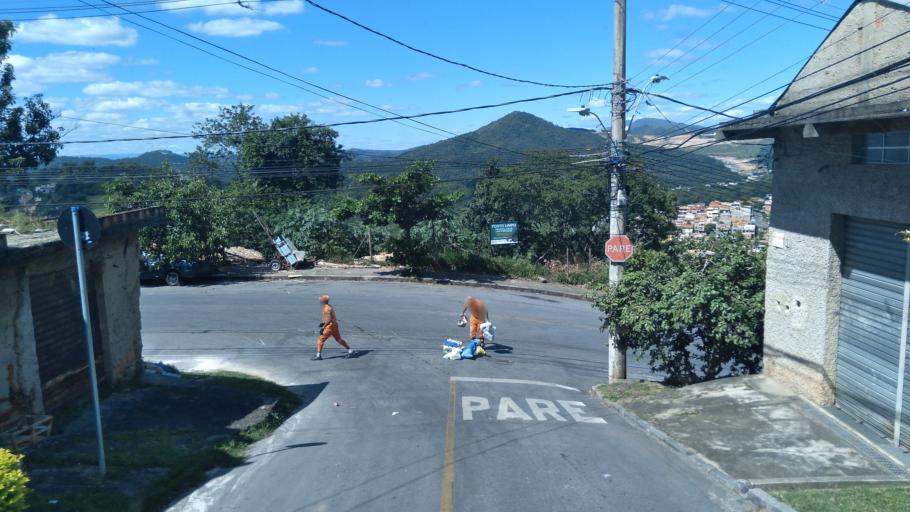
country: BR
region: Minas Gerais
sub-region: Belo Horizonte
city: Belo Horizonte
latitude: -19.8574
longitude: -43.8811
